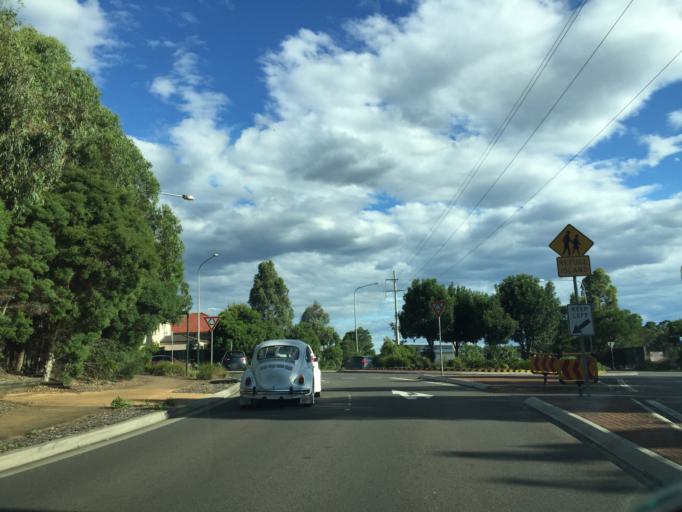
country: AU
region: New South Wales
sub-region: The Hills Shire
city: Glenhaven
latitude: -33.7090
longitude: 150.9739
